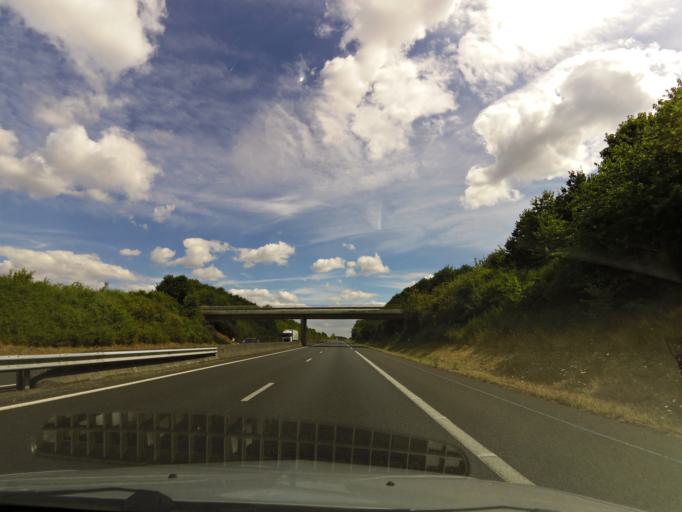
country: FR
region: Pays de la Loire
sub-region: Departement de la Vendee
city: Les Brouzils
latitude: 46.9042
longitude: -1.3126
